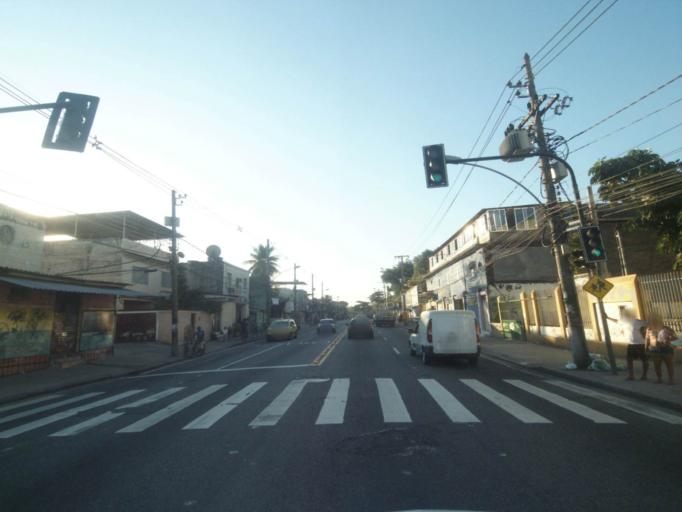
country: BR
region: Rio de Janeiro
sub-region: Sao Joao De Meriti
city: Sao Joao de Meriti
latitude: -22.9510
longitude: -43.3588
